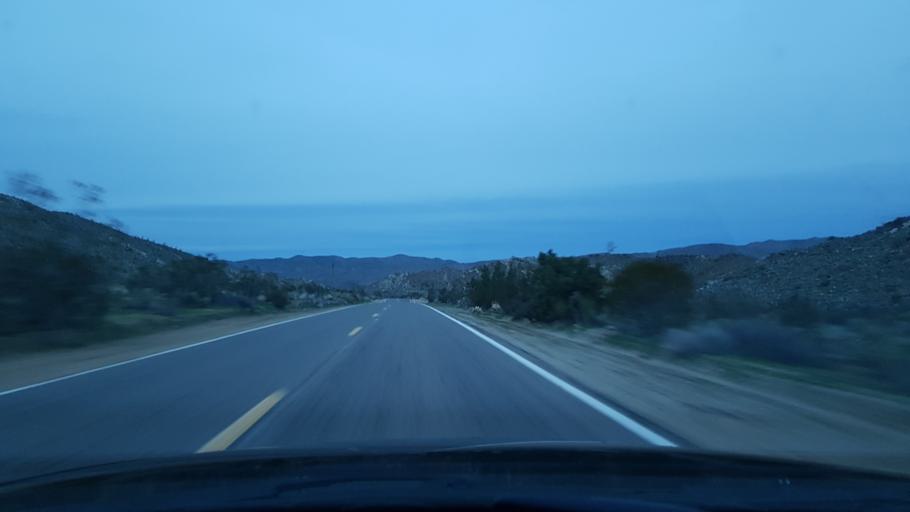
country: US
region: California
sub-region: San Diego County
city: Julian
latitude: 33.0311
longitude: -116.4135
